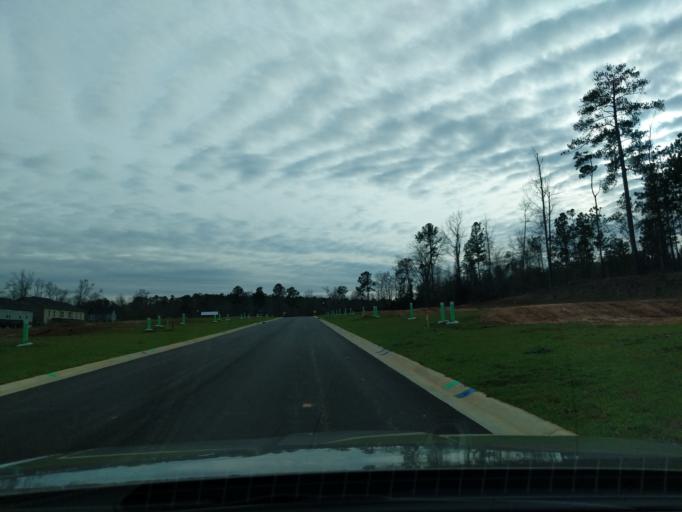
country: US
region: Georgia
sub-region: Columbia County
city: Grovetown
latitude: 33.4670
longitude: -82.2039
